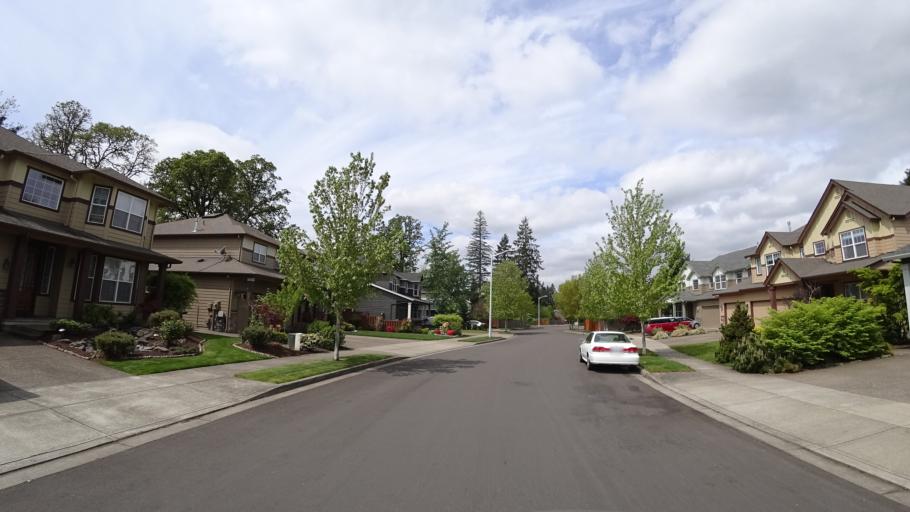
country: US
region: Oregon
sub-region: Washington County
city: Hillsboro
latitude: 45.5464
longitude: -122.9966
